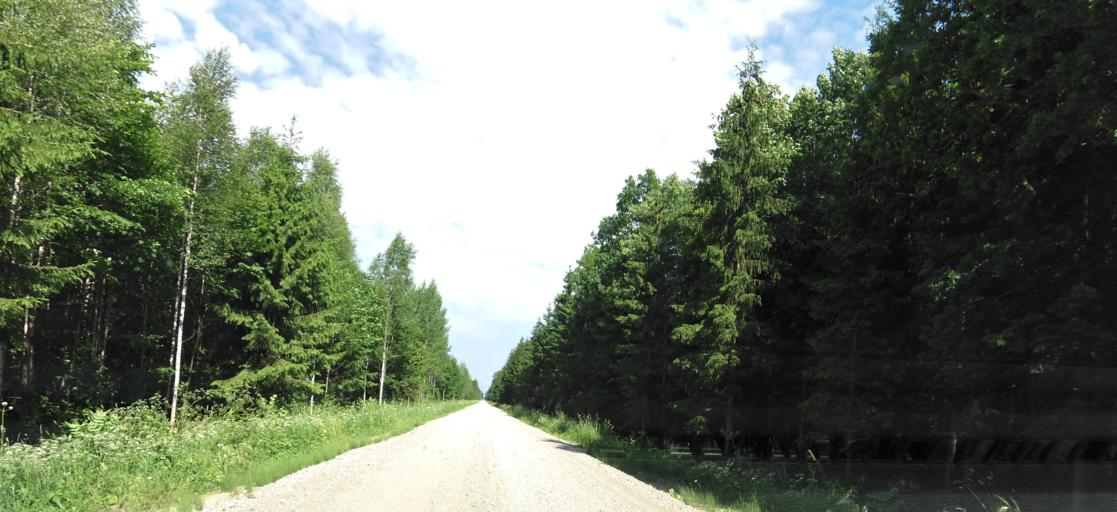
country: LT
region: Panevezys
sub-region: Birzai
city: Birzai
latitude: 56.2313
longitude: 24.9916
